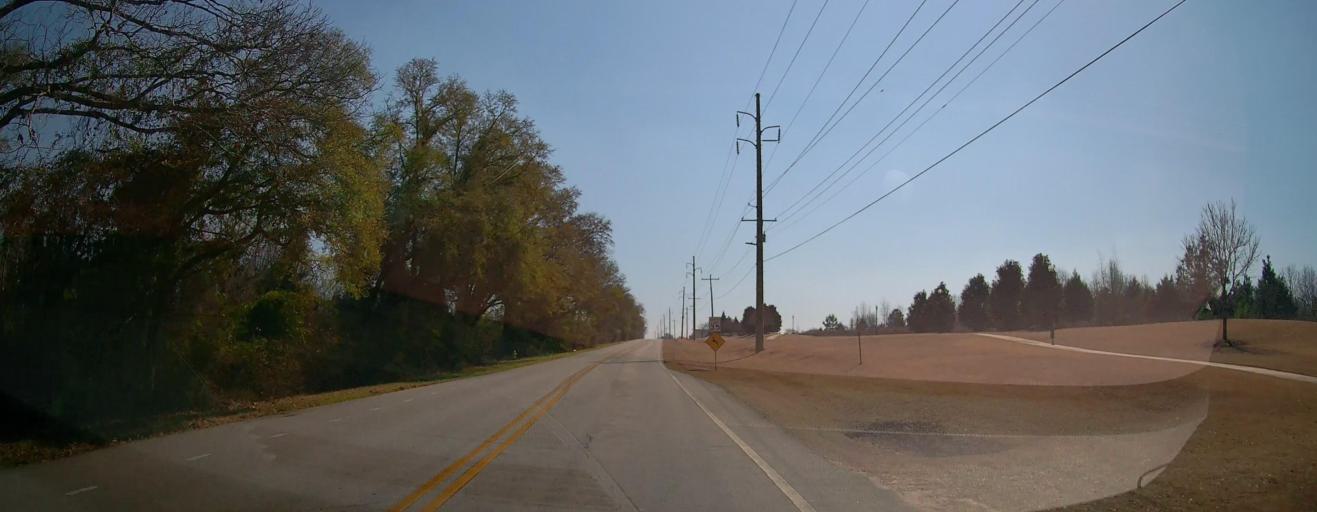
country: US
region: Georgia
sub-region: Houston County
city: Perry
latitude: 32.4801
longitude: -83.7589
